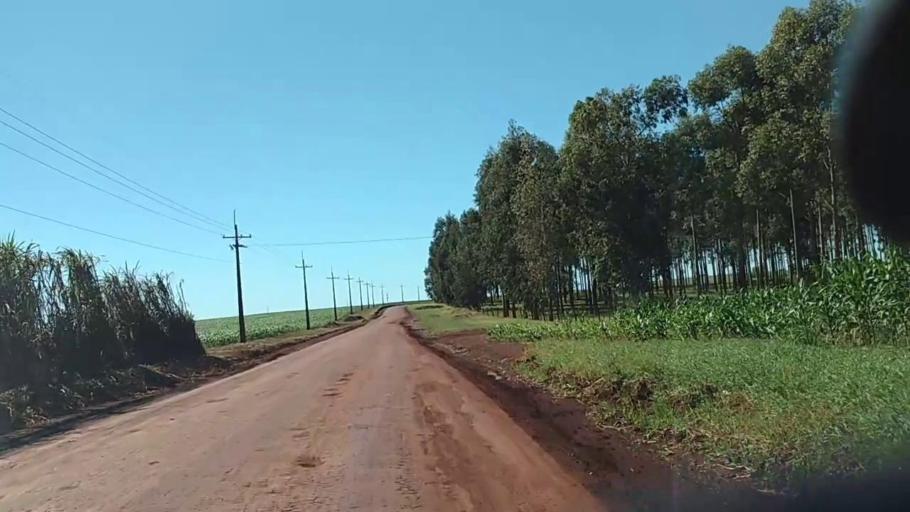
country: PY
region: Alto Parana
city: Naranjal
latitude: -25.9403
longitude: -55.3029
